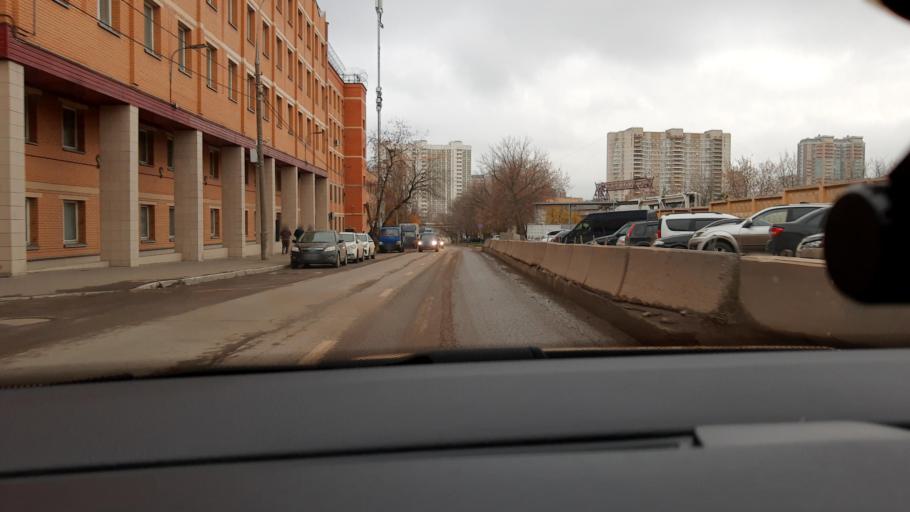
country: RU
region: Moscow
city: Kozeyevo
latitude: 55.8828
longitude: 37.6299
